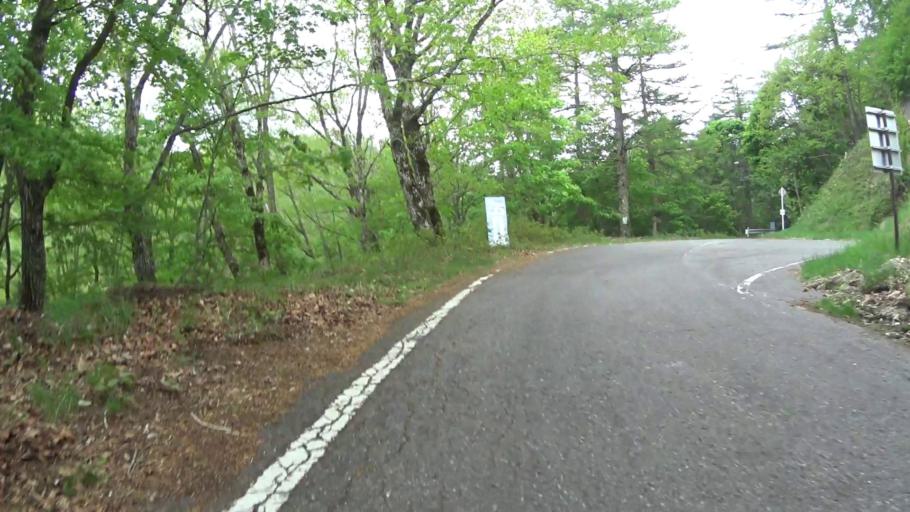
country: JP
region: Yamanashi
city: Kofu-shi
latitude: 35.8334
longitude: 138.5688
